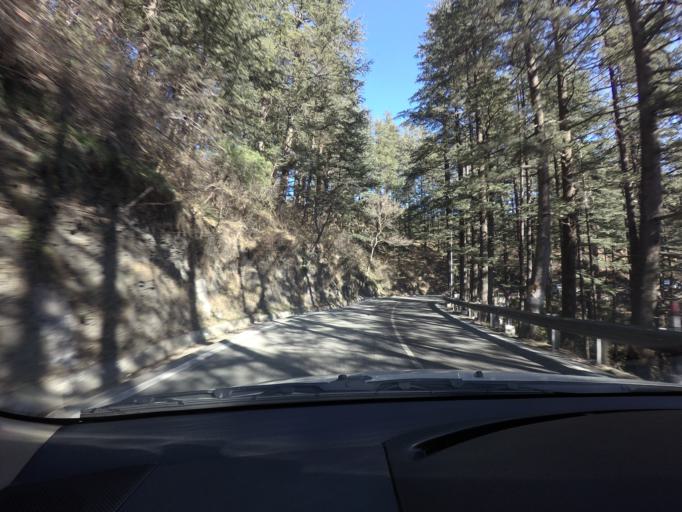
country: IN
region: Himachal Pradesh
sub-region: Shimla
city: Shimla
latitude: 31.1125
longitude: 77.2205
